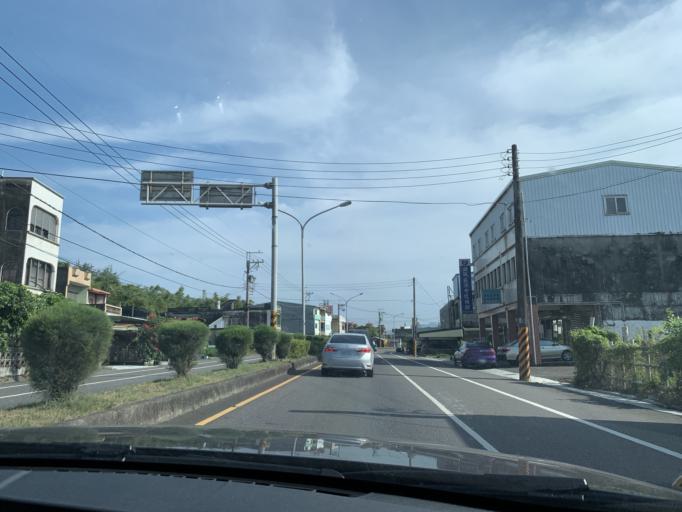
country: TW
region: Taiwan
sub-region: Yilan
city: Yilan
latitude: 24.7636
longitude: 121.8158
